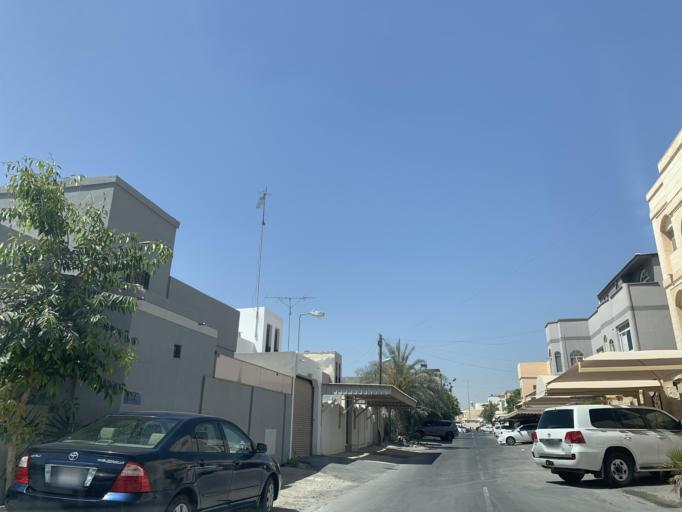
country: BH
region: Northern
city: Ar Rifa'
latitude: 26.1361
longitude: 50.5798
